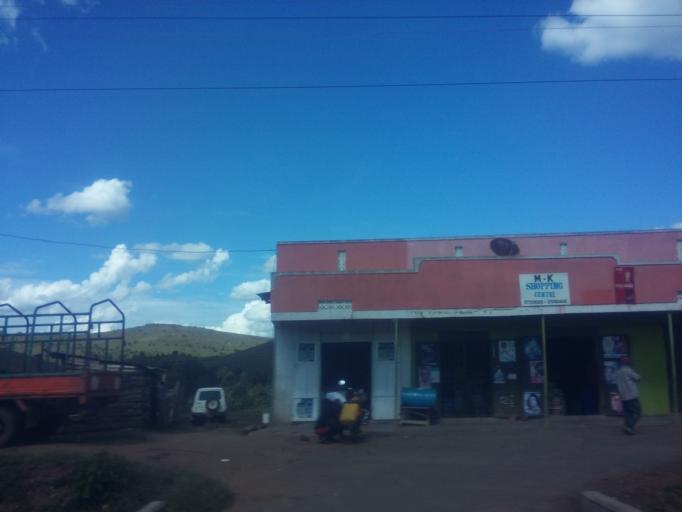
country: UG
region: Western Region
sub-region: Ntungamo District
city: Ntungamo
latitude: -0.9625
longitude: 30.2052
